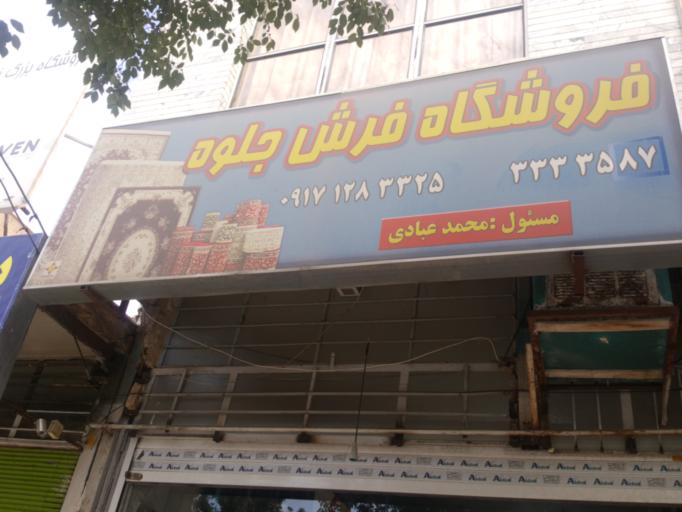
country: IR
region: Fars
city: Marvdasht
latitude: 29.8821
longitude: 52.8099
